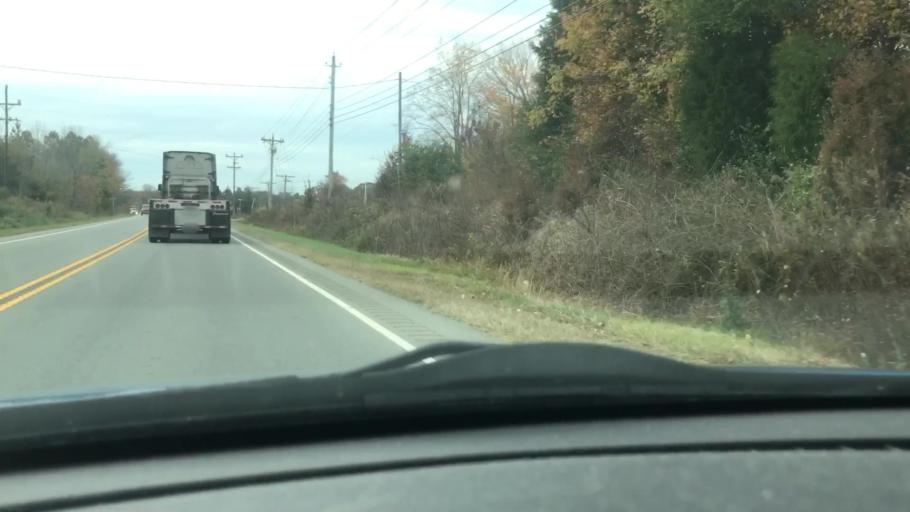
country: US
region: North Carolina
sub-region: Davidson County
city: Lexington
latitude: 35.8011
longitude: -80.1568
